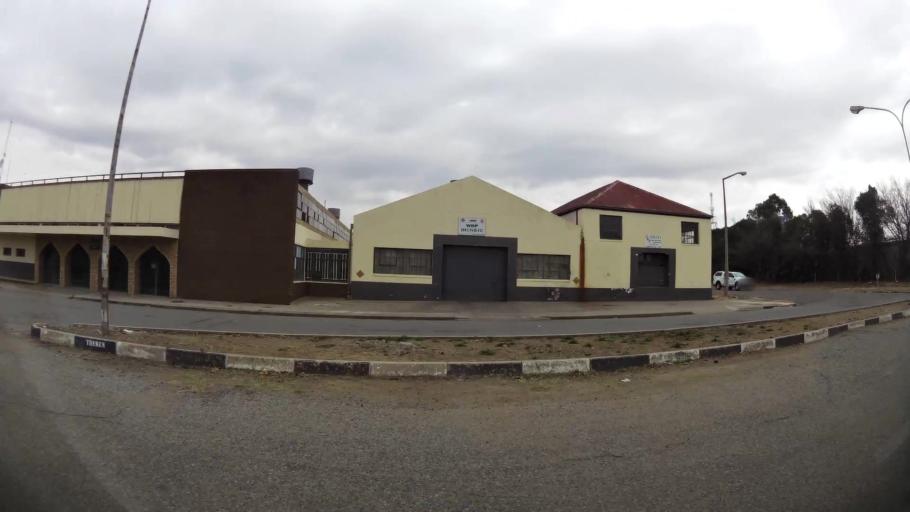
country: ZA
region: Orange Free State
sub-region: Fezile Dabi District Municipality
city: Kroonstad
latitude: -27.6596
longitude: 27.2376
